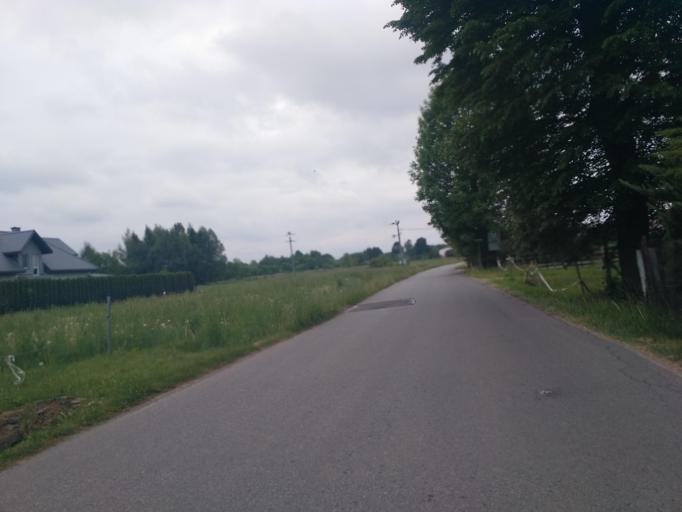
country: PL
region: Subcarpathian Voivodeship
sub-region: Krosno
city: Krosno
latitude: 49.6745
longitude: 21.7331
